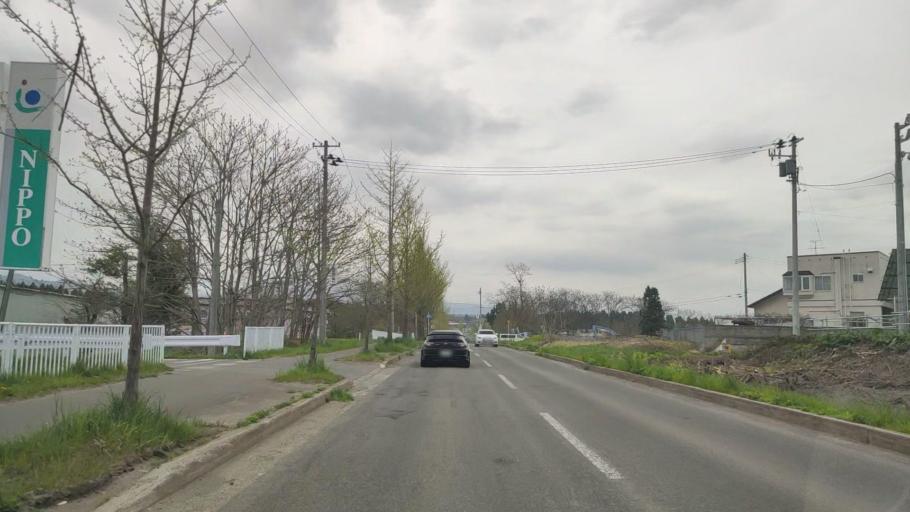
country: JP
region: Aomori
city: Aomori Shi
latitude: 40.7957
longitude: 140.7849
